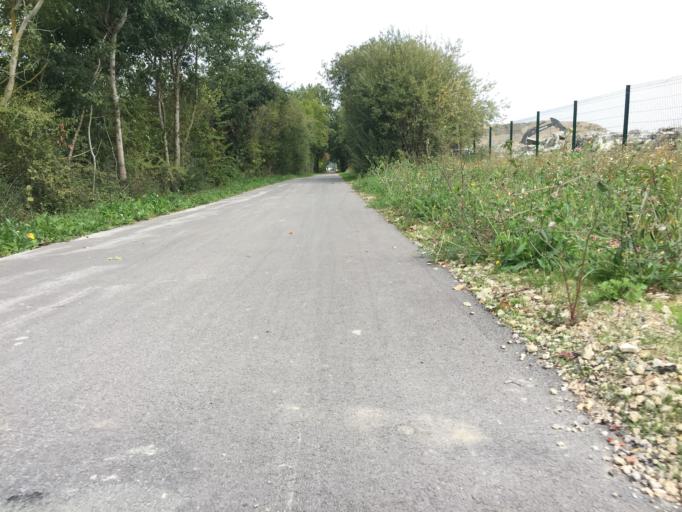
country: FR
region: Picardie
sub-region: Departement de l'Oise
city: Auneuil
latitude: 49.3827
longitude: 1.9946
